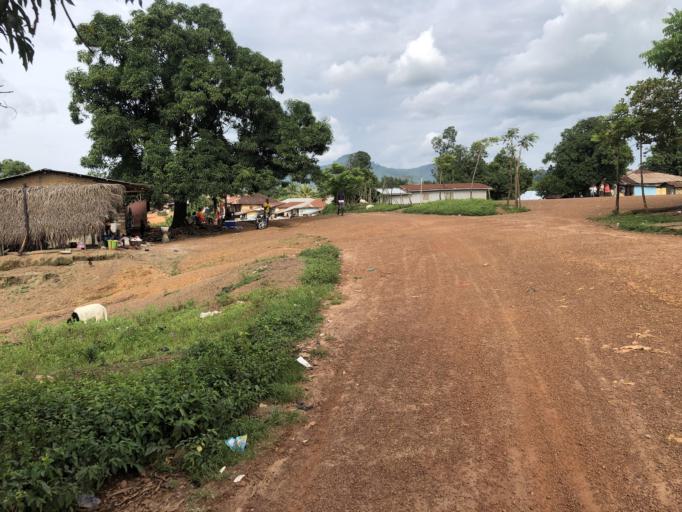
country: SL
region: Northern Province
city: Masaka
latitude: 8.7481
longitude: -11.8415
